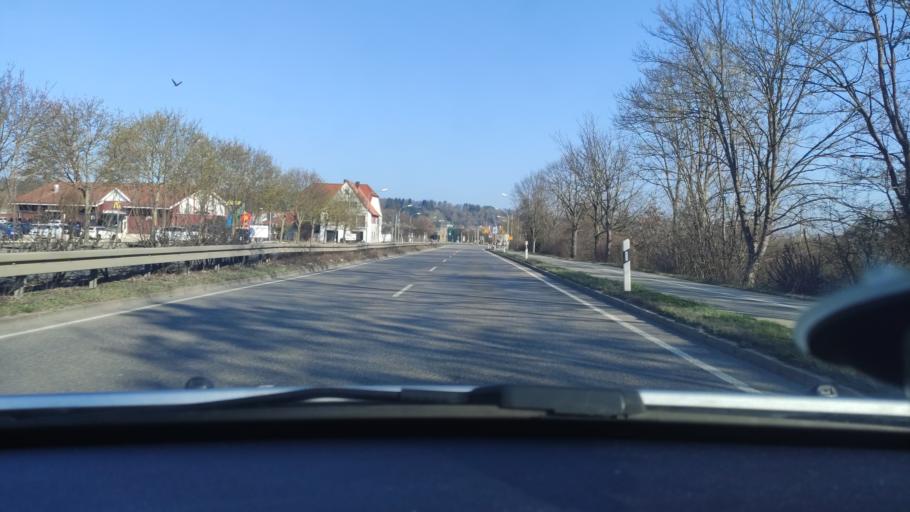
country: DE
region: Baden-Wuerttemberg
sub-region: Tuebingen Region
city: Balingen
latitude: 48.2610
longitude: 8.8539
